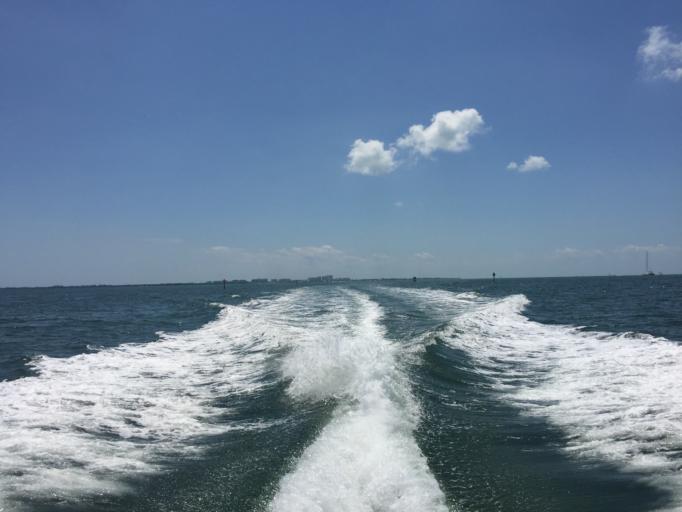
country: US
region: Florida
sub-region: Miami-Dade County
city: Coconut Grove
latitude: 25.7230
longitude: -80.2195
